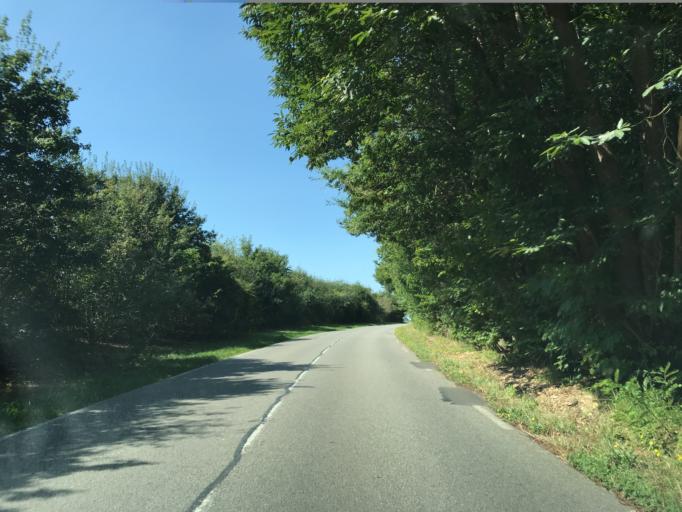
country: FR
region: Haute-Normandie
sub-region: Departement de l'Eure
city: La Chapelle-Reanville
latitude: 49.0942
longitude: 1.3943
